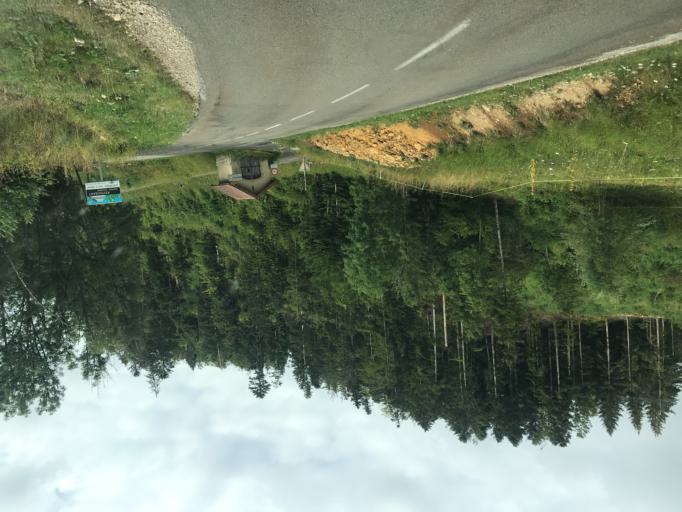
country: FR
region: Franche-Comte
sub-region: Departement du Jura
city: Valfin-les-Saint-Claude
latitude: 46.4716
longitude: 5.8371
